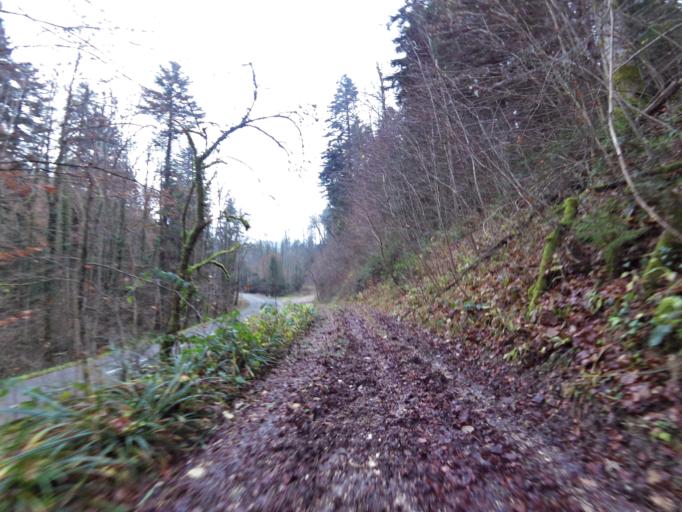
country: FR
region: Alsace
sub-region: Departement du Haut-Rhin
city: Ferrette
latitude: 47.4337
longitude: 7.2940
